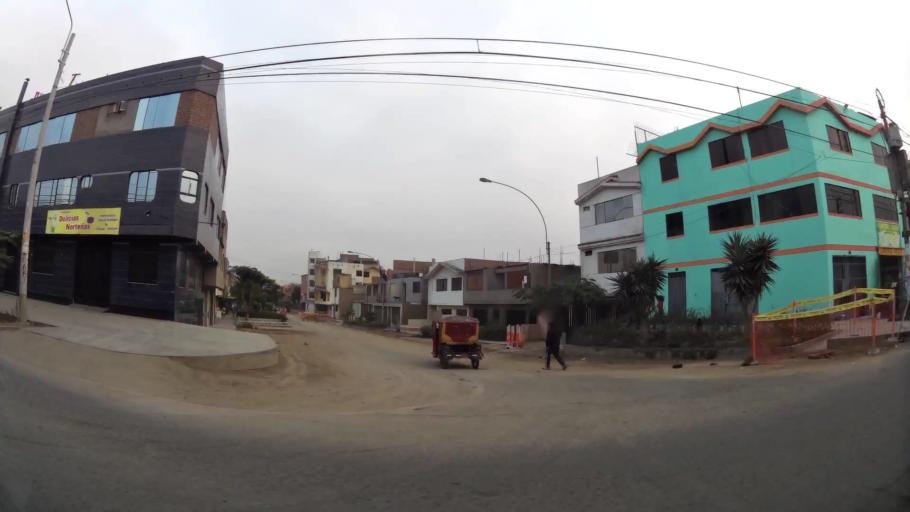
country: PE
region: Lima
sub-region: Lima
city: Independencia
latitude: -11.9913
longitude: -77.0027
